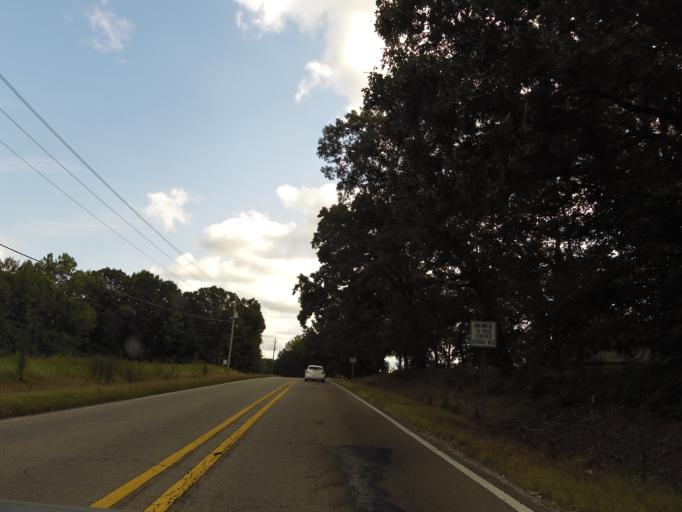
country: US
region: Mississippi
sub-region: Alcorn County
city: Farmington
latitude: 34.9937
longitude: -88.4631
